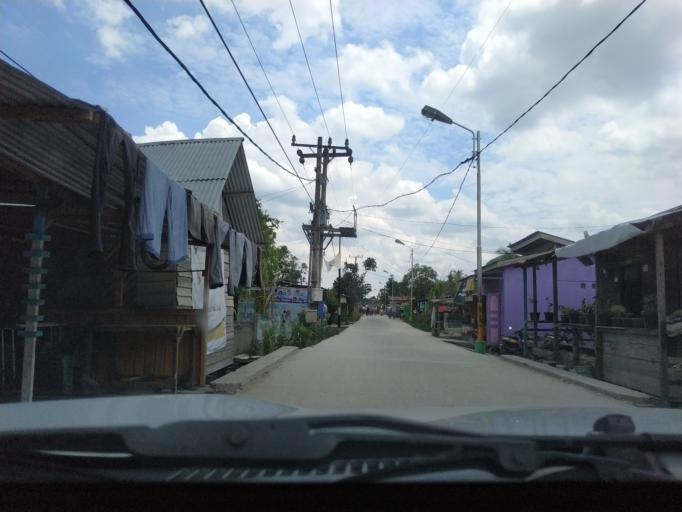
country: ID
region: North Sumatra
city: Tanjungbalai
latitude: 2.9599
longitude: 99.8139
